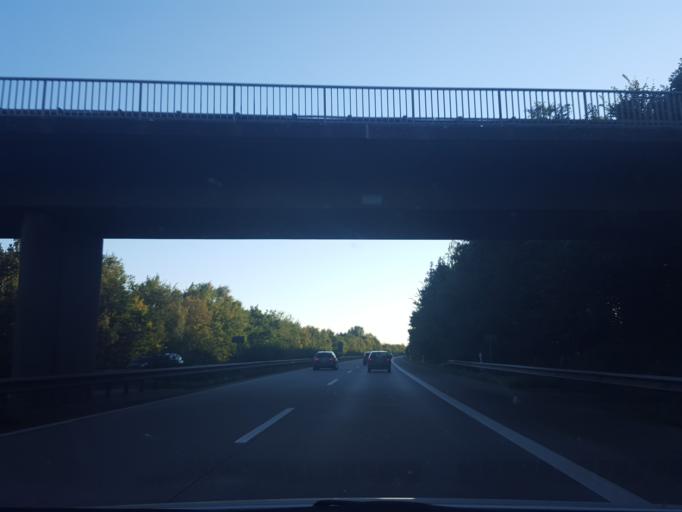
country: DE
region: Lower Saxony
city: Loxstedt
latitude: 53.4840
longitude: 8.6209
